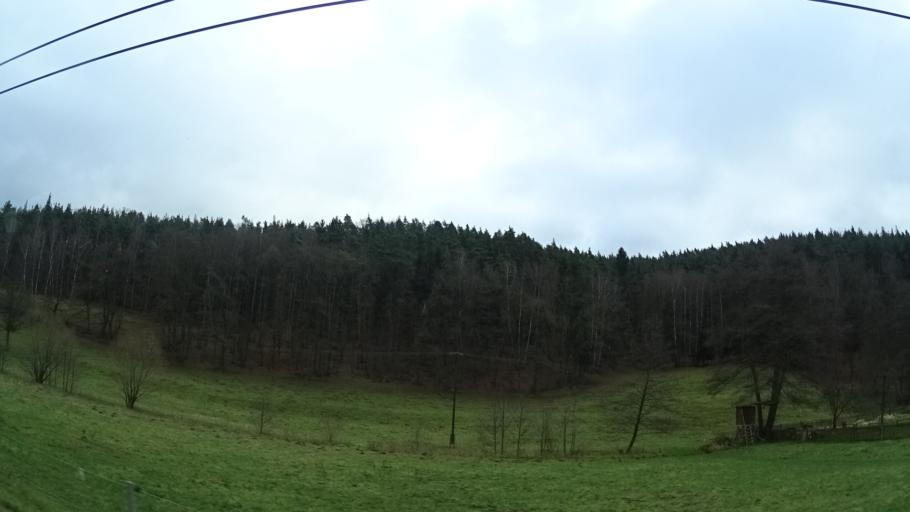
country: DE
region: Thuringia
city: Herschdorf
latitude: 50.7214
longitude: 11.5032
